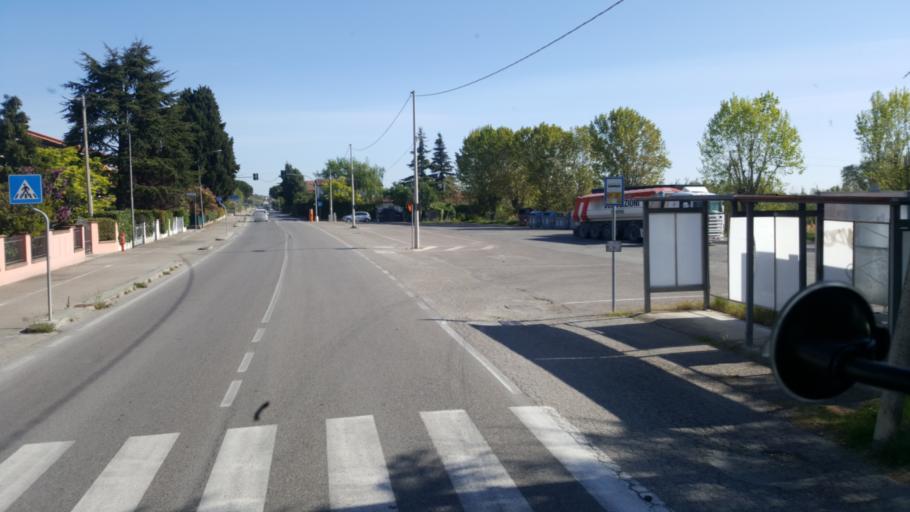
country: IT
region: Emilia-Romagna
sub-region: Provincia di Rimini
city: Poggio Berni
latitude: 44.0145
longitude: 12.4083
